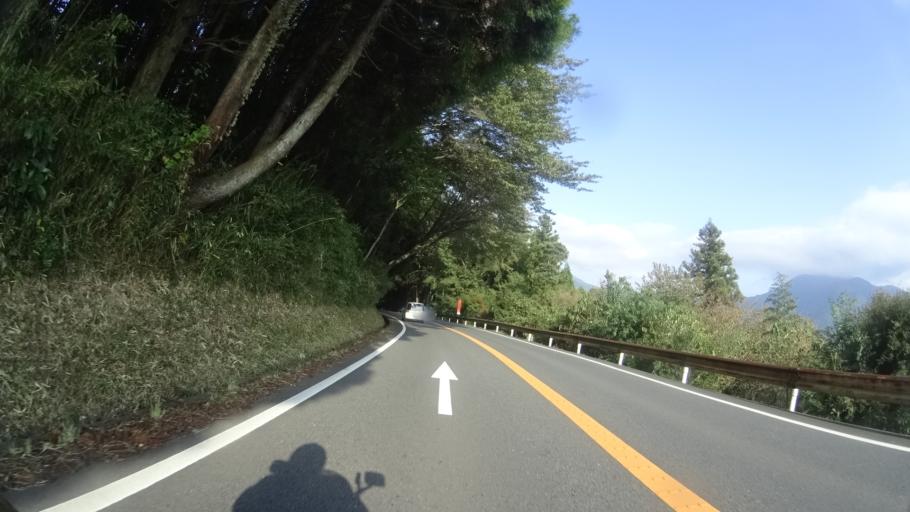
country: JP
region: Oita
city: Beppu
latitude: 33.2640
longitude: 131.3354
